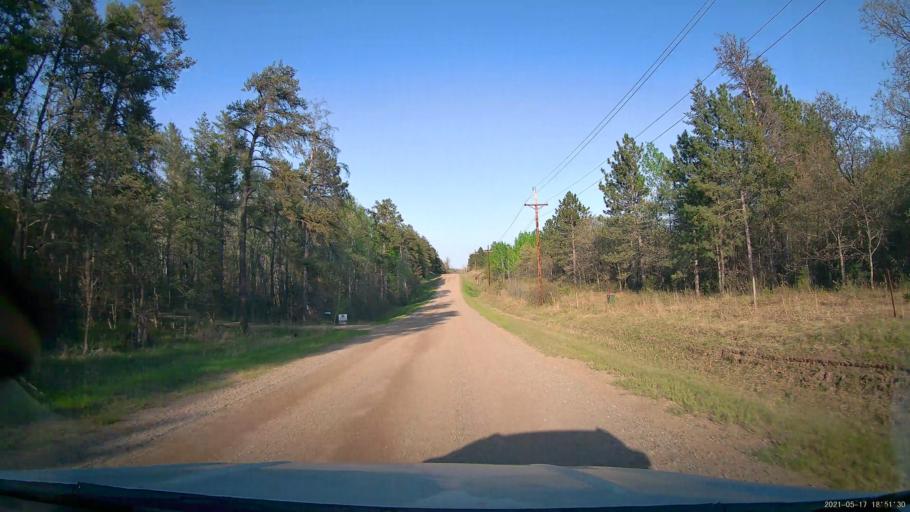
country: US
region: Minnesota
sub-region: Hubbard County
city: Park Rapids
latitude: 46.9437
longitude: -95.0119
